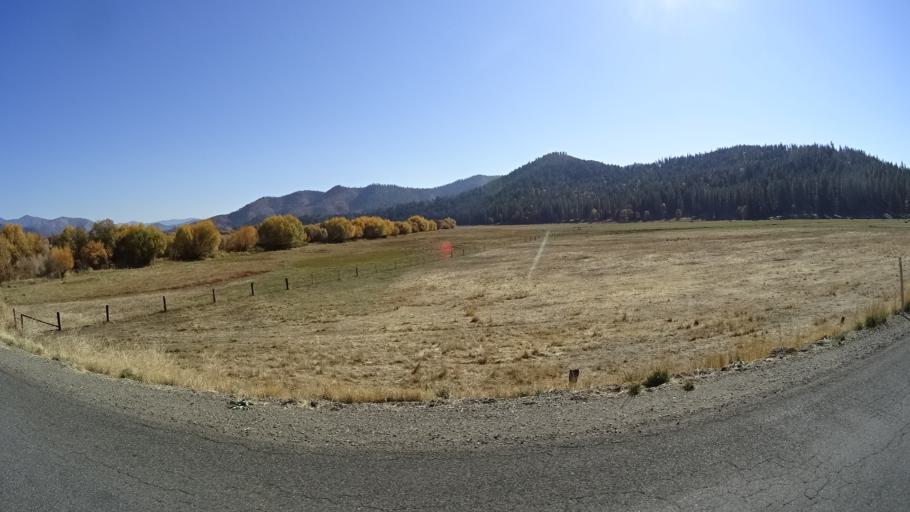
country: US
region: California
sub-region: Siskiyou County
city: Yreka
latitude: 41.6283
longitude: -122.9578
